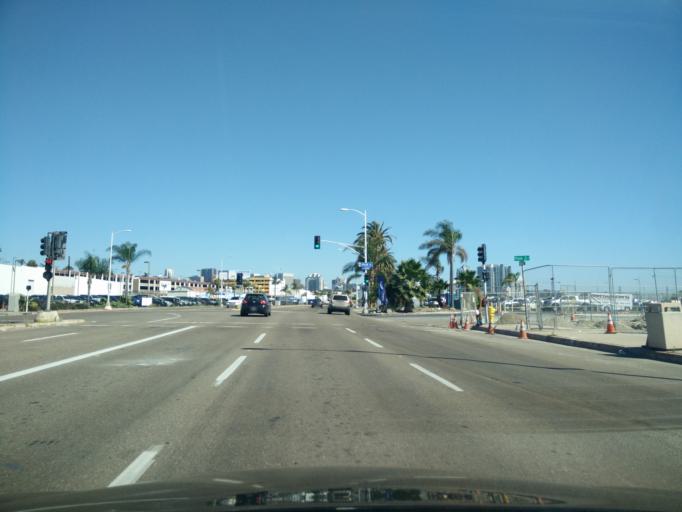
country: US
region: California
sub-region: San Diego County
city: San Diego
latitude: 32.7328
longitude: -117.1757
